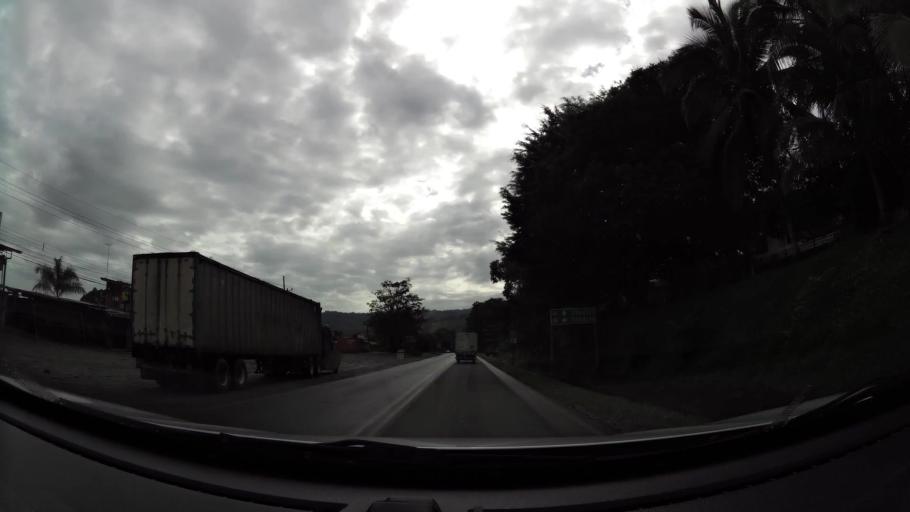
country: CR
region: Limon
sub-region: Canton de Siquirres
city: Siquirres
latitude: 10.0970
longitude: -83.5134
